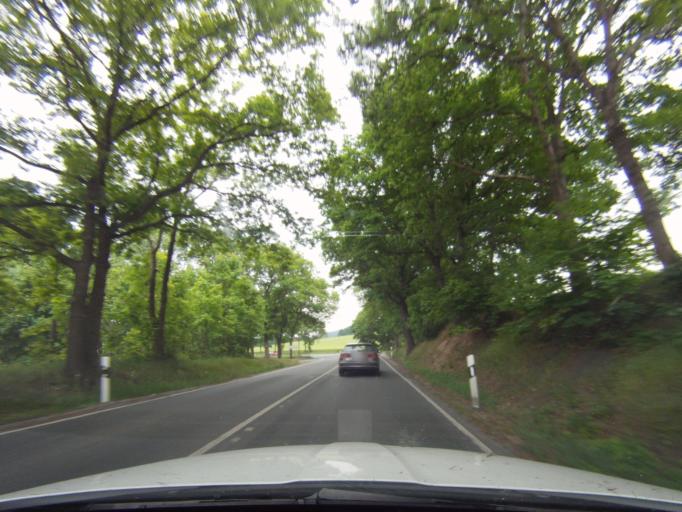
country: DE
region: Thuringia
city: Bad Blankenburg
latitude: 50.6733
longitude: 11.3202
